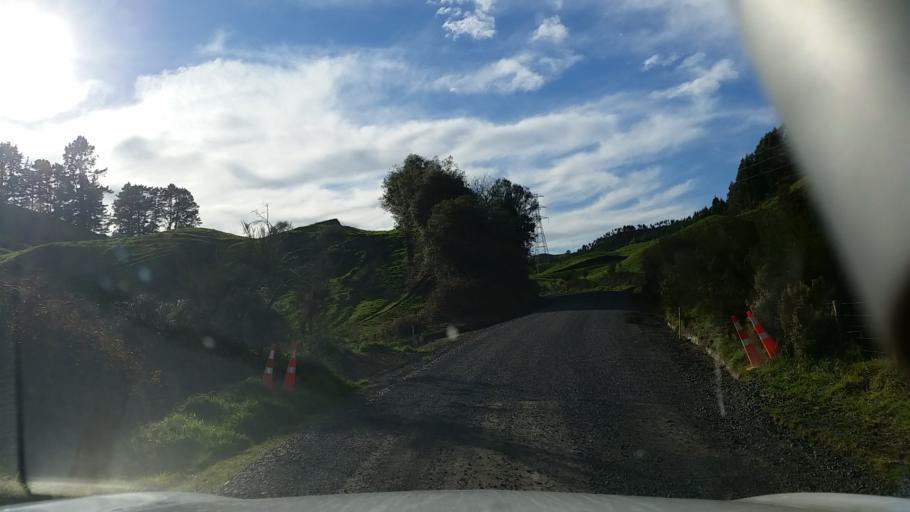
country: NZ
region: Waikato
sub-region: South Waikato District
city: Tokoroa
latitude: -38.3630
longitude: 176.0906
